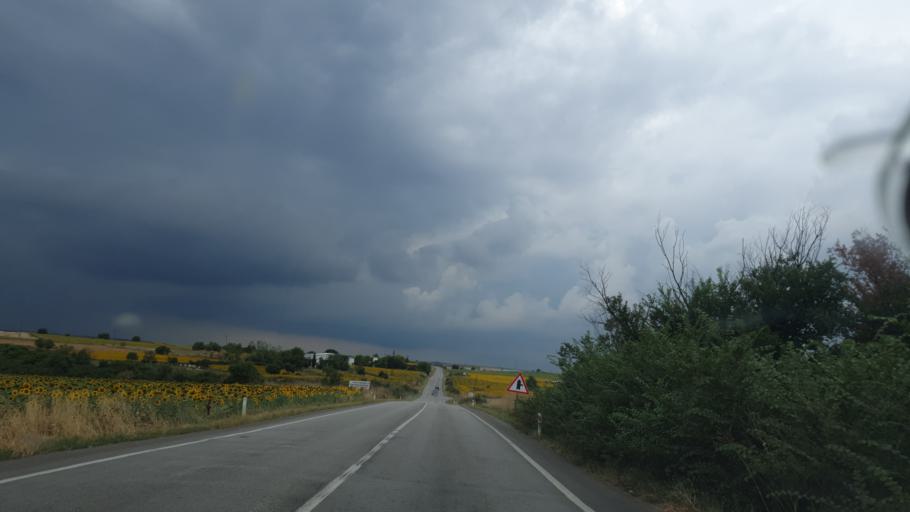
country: TR
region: Tekirdag
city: Hayrabolu
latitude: 41.2192
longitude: 27.0774
